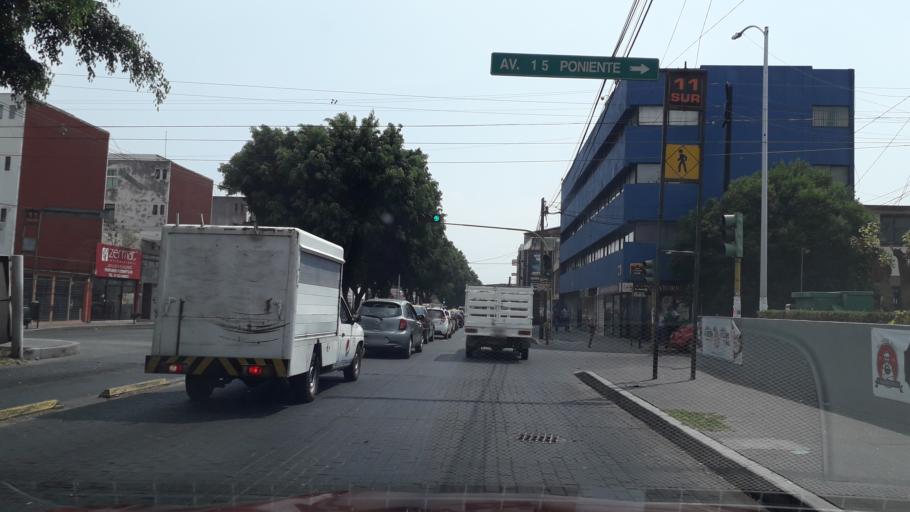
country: MX
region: Puebla
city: Puebla
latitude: 19.0433
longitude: -98.2093
